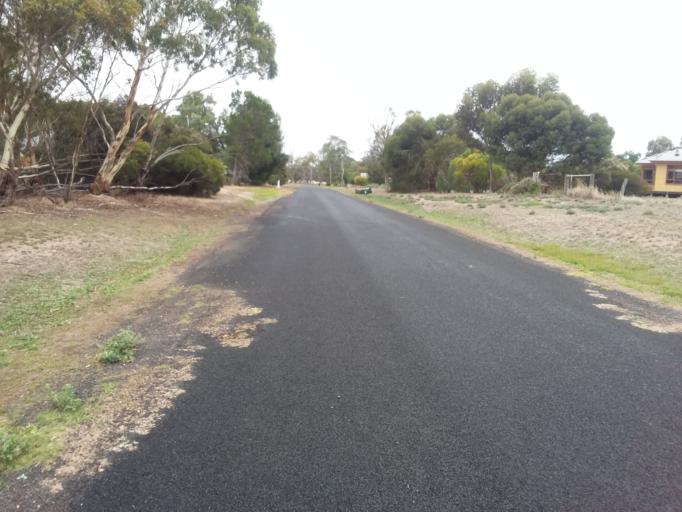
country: AU
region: Victoria
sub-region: Horsham
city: Horsham
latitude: -36.7413
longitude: 141.9369
